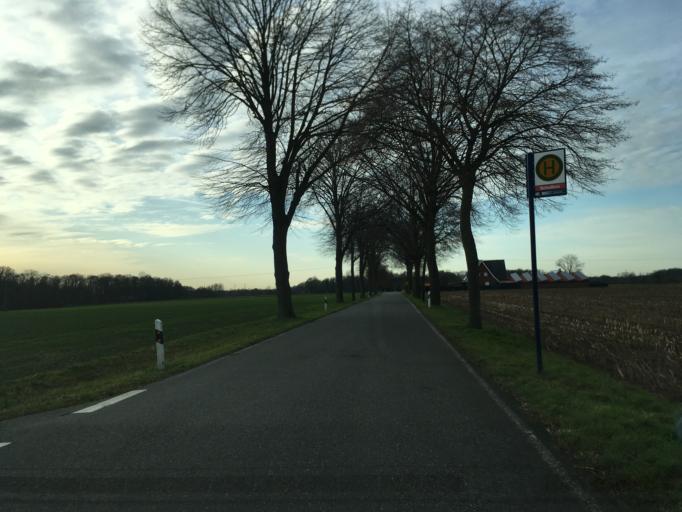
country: DE
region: North Rhine-Westphalia
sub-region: Regierungsbezirk Munster
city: Gescher
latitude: 51.9877
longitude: 7.0367
